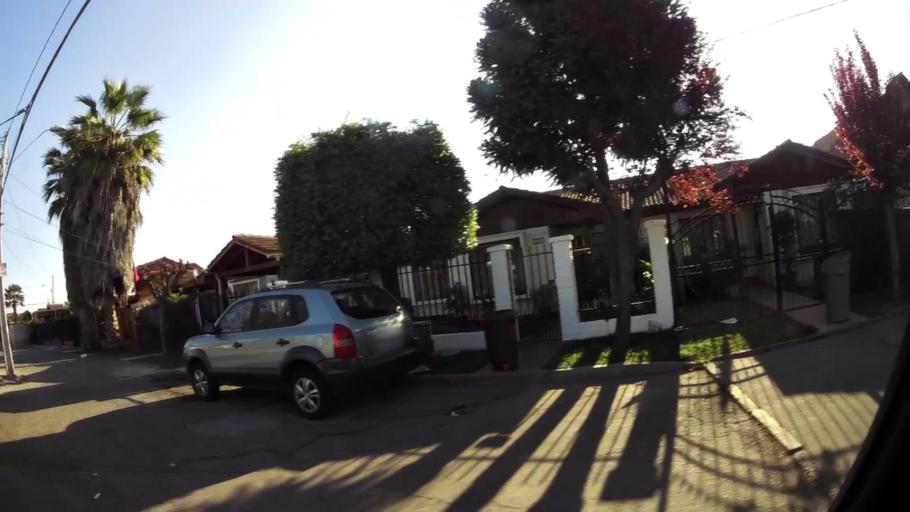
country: CL
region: Santiago Metropolitan
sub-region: Provincia de Santiago
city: Lo Prado
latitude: -33.4838
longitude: -70.7569
